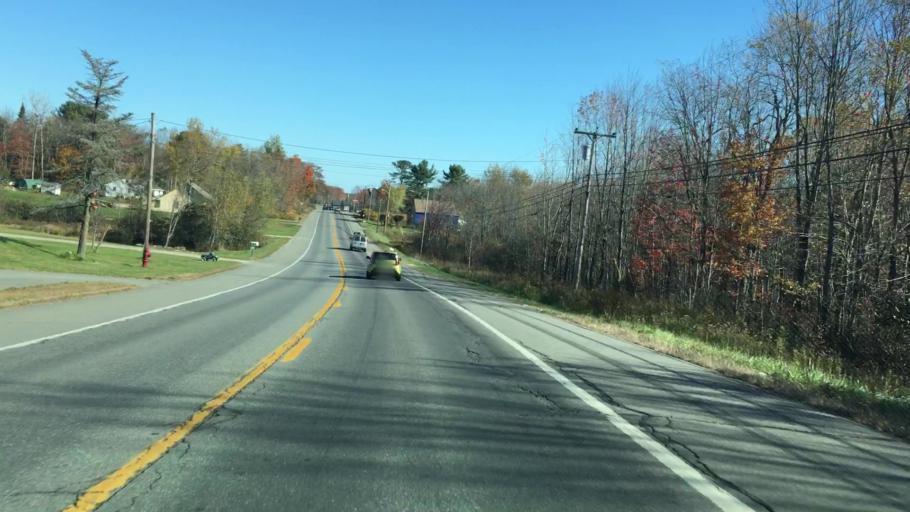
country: US
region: Maine
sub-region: Waldo County
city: Stockton Springs
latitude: 44.4761
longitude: -68.8803
